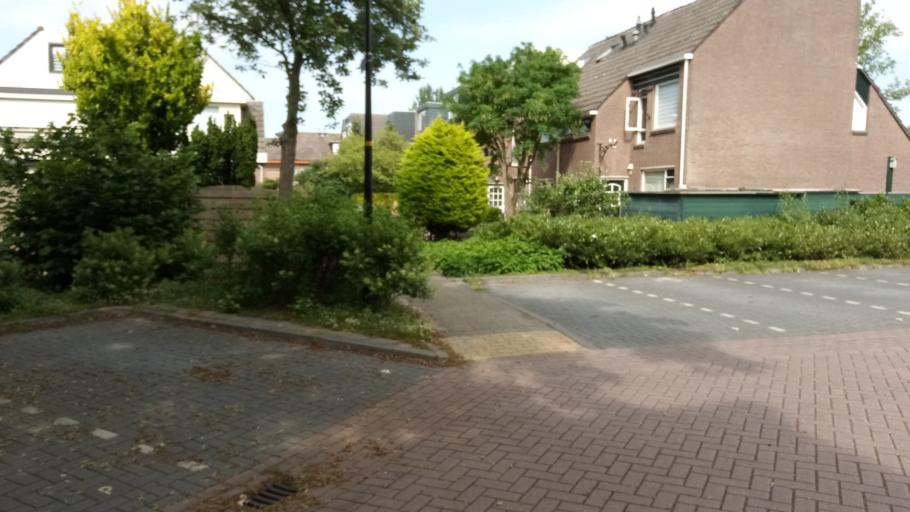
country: NL
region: North Holland
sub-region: Gemeente Langedijk
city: Broek op Langedijk
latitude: 52.6672
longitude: 4.8258
